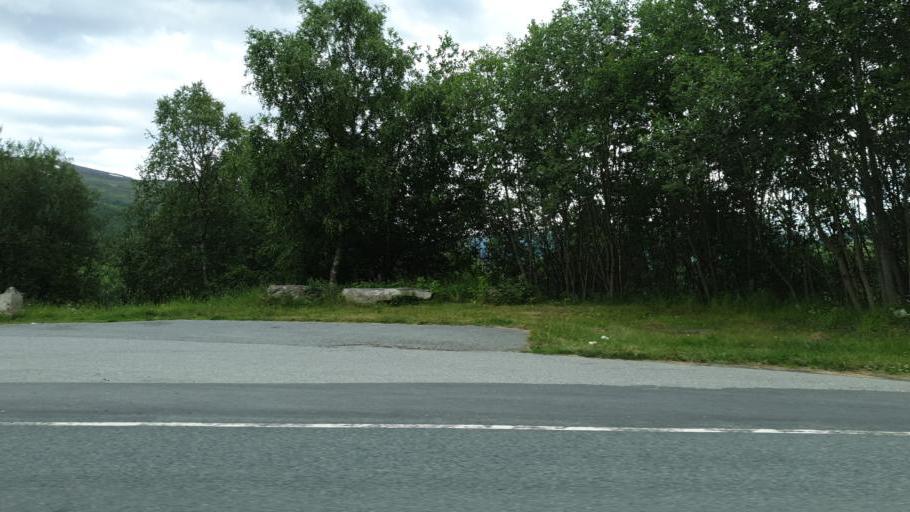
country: NO
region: Sor-Trondelag
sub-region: Oppdal
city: Oppdal
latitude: 62.5101
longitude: 9.5968
